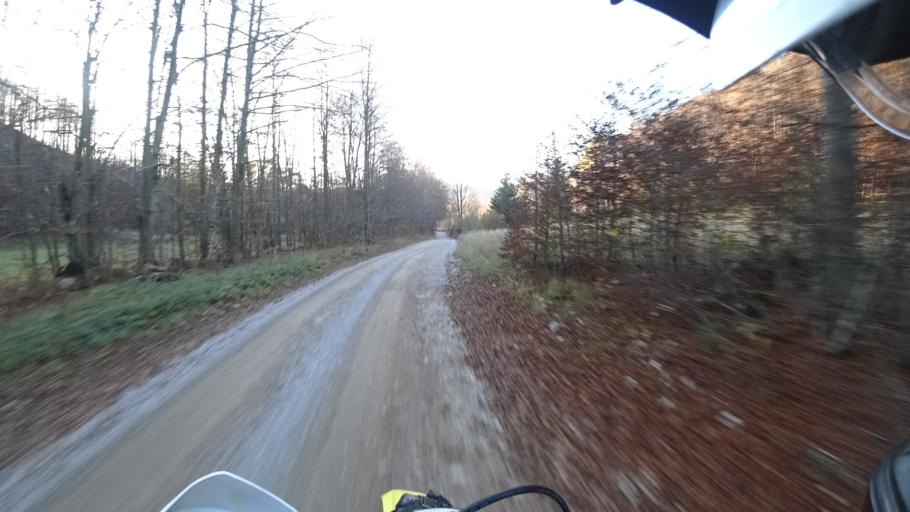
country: HR
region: Primorsko-Goranska
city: Klana
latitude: 45.5018
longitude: 14.4408
